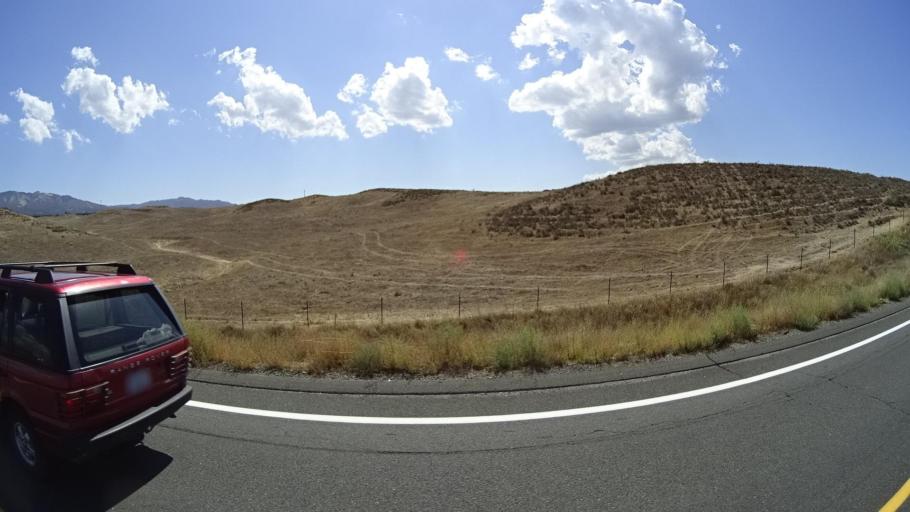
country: US
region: California
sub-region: San Diego County
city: Julian
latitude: 33.2648
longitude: -116.6588
